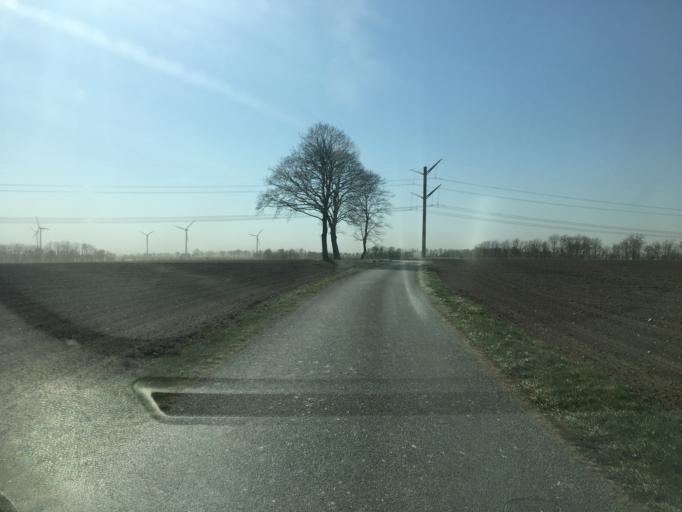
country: DK
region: South Denmark
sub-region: Aabenraa Kommune
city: Rodekro
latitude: 55.1097
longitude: 9.2173
